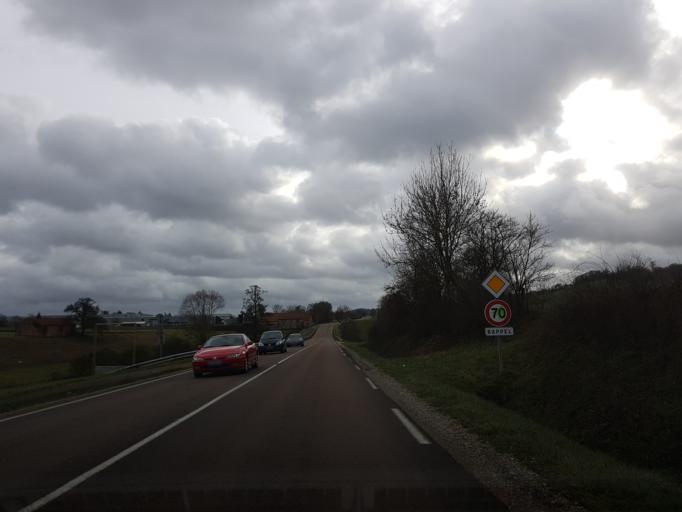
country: FR
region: Champagne-Ardenne
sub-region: Departement de la Haute-Marne
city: Langres
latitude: 47.8622
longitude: 5.3429
